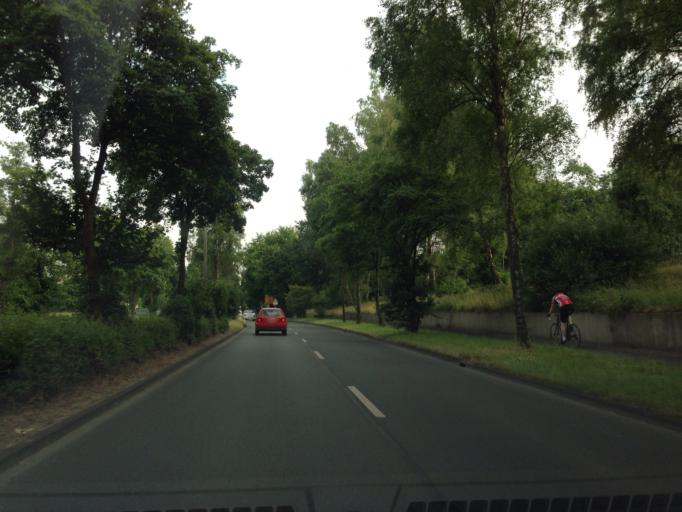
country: DE
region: North Rhine-Westphalia
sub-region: Regierungsbezirk Munster
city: Muenster
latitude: 51.9525
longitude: 7.6033
